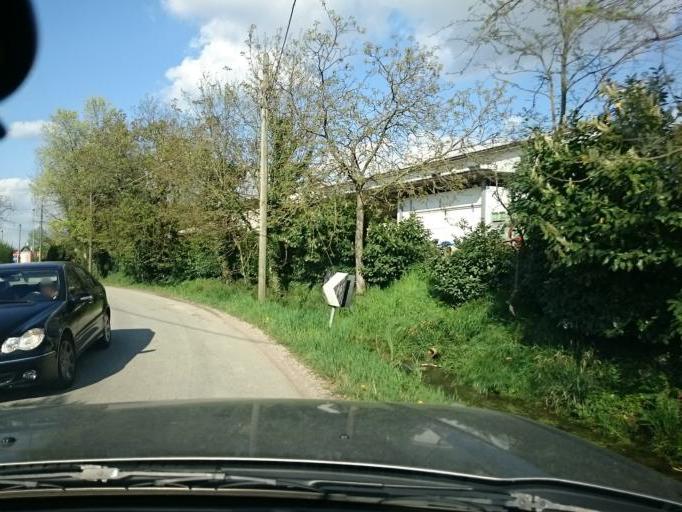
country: IT
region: Veneto
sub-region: Provincia di Padova
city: Trebaseleghe
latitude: 45.6012
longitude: 12.0309
